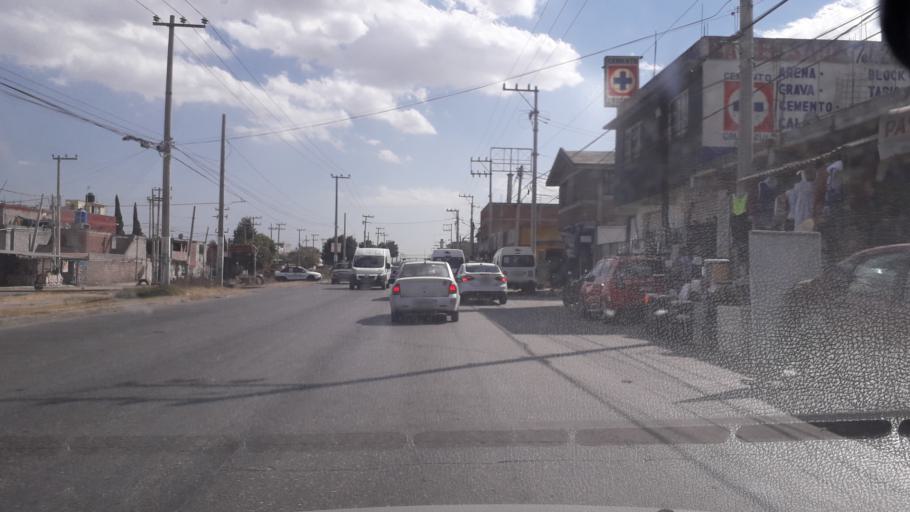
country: MX
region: Mexico
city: Ecatepec
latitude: 19.6317
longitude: -99.0529
